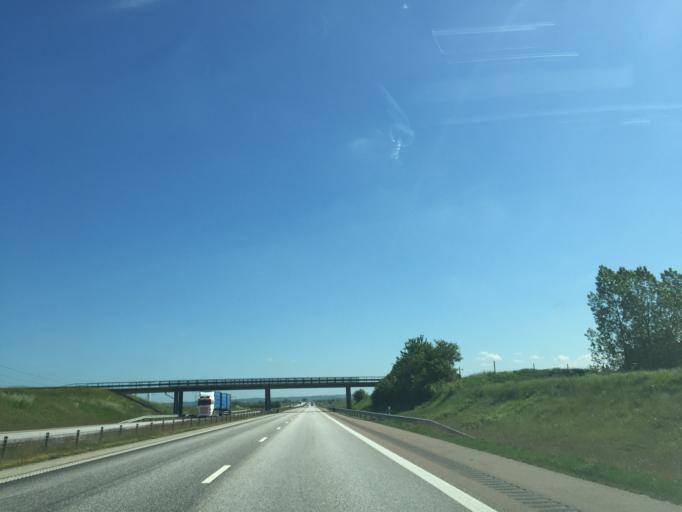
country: SE
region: Skane
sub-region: Astorps Kommun
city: Astorp
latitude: 56.1584
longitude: 12.9584
